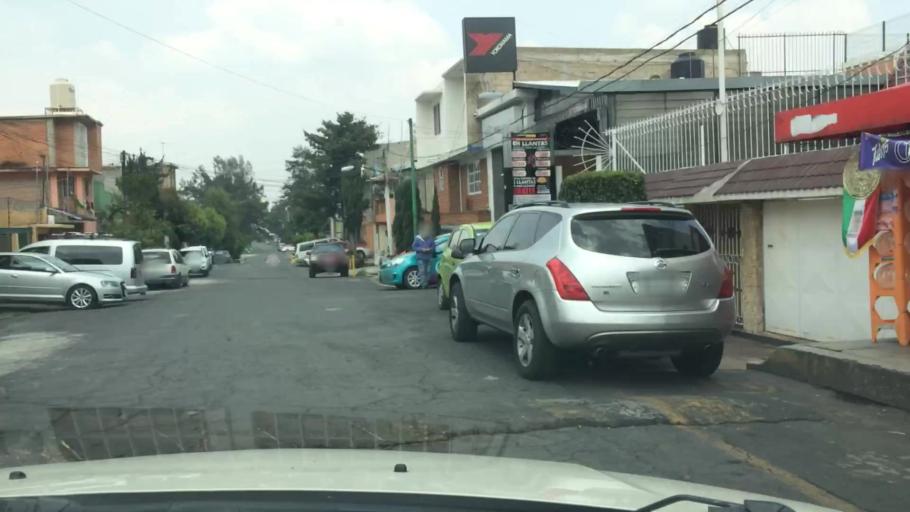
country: MX
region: Mexico City
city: Magdalena Contreras
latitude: 19.2905
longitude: -99.2248
